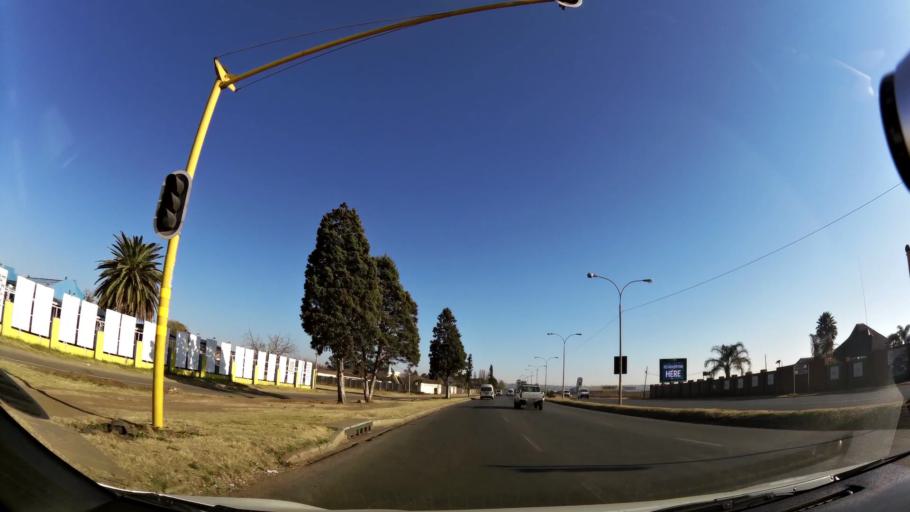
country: ZA
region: Gauteng
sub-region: Ekurhuleni Metropolitan Municipality
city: Germiston
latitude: -26.2863
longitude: 28.1333
